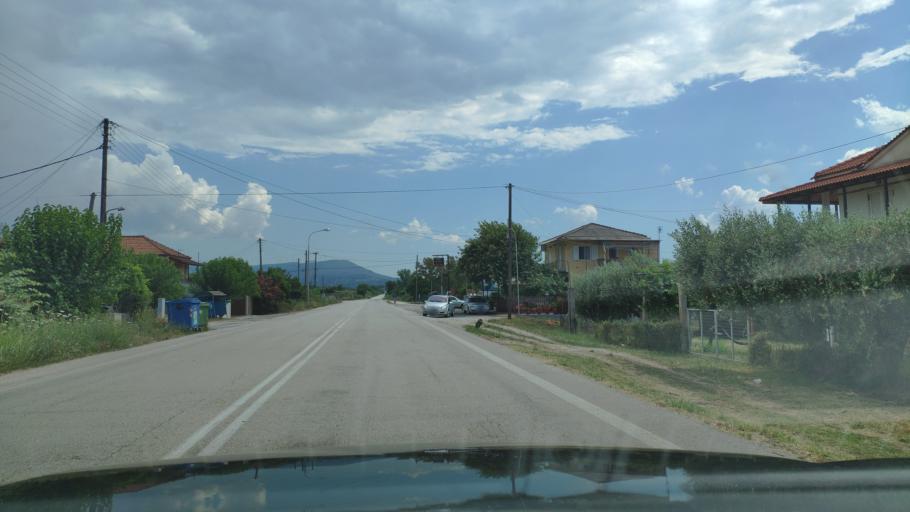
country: GR
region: West Greece
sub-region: Nomos Aitolias kai Akarnanias
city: Krikellos
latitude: 38.9444
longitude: 21.1766
